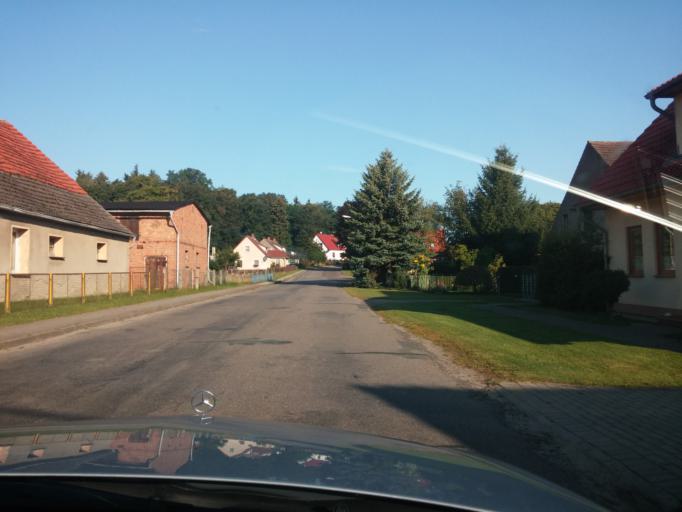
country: DE
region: Brandenburg
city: Putlitz
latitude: 53.2867
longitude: 12.0483
